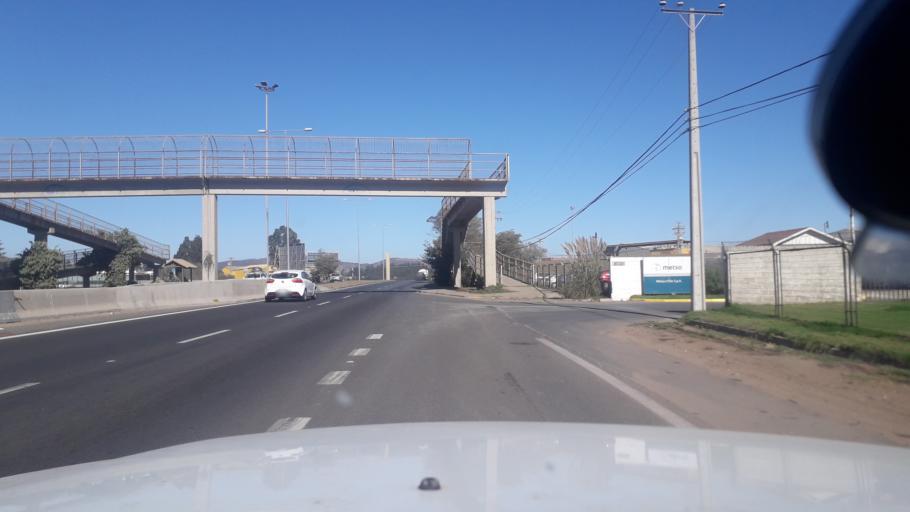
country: CL
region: Valparaiso
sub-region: Provincia de Valparaiso
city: Vina del Mar
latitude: -32.9589
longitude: -71.5100
